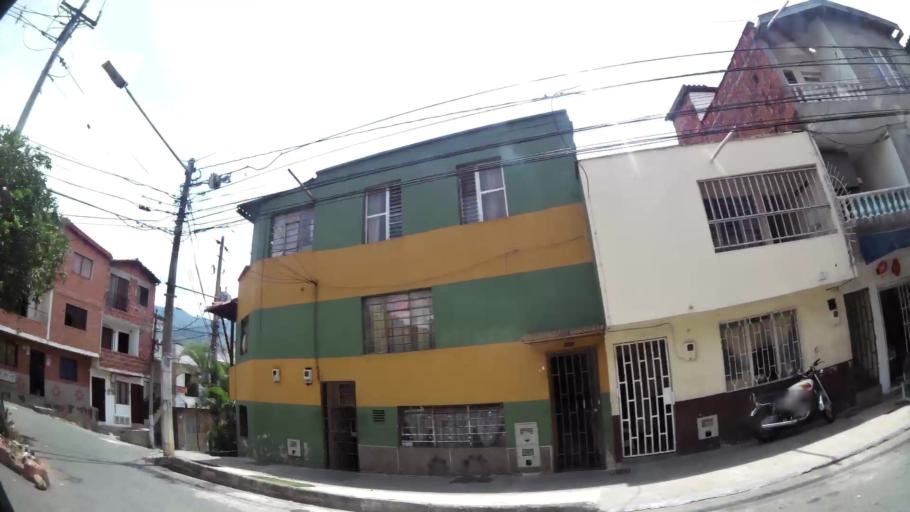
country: CO
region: Antioquia
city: Bello
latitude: 6.3333
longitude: -75.5607
